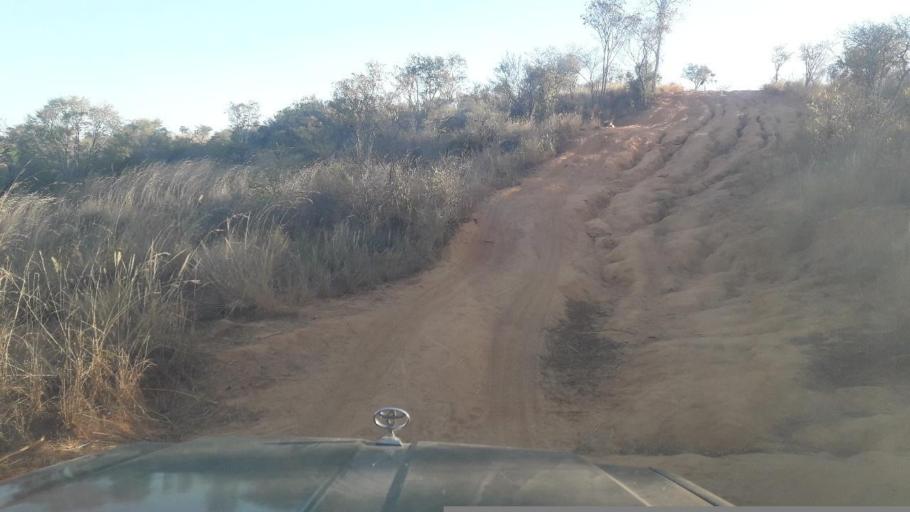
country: MG
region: Boeny
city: Sitampiky
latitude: -16.4970
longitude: 45.6078
